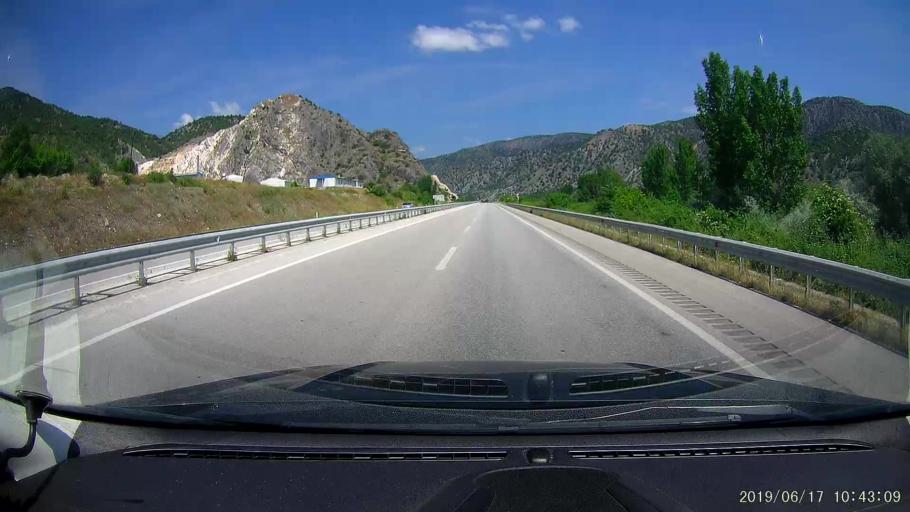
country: TR
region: Corum
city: Kargi
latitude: 41.0594
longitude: 34.5407
